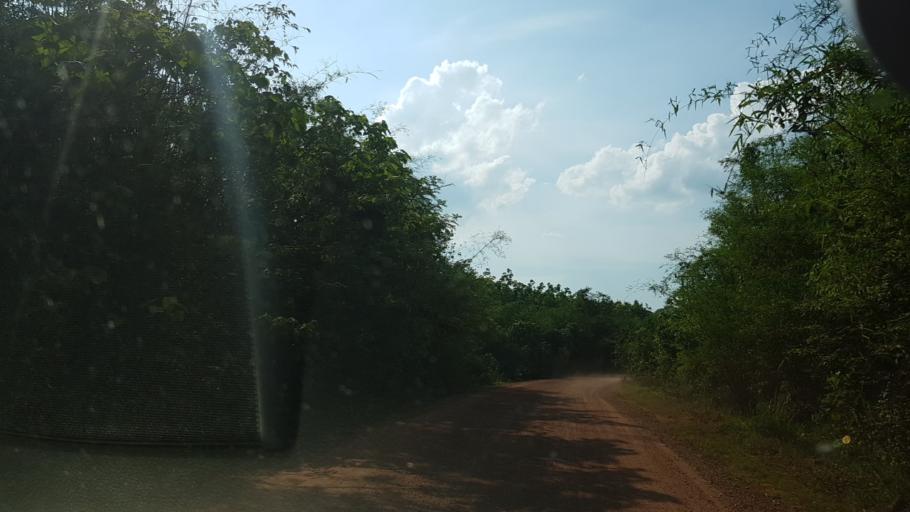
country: LA
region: Vientiane
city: Muang Phon-Hong
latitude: 18.3495
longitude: 102.2820
